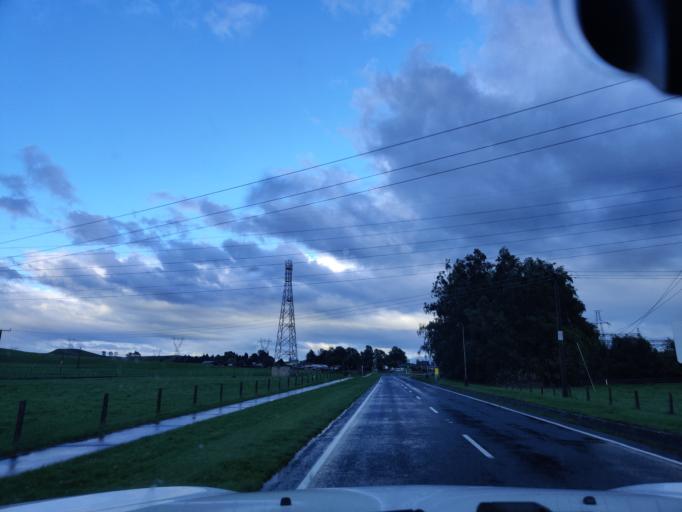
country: NZ
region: Waikato
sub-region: South Waikato District
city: Tokoroa
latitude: -38.4206
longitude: 175.8025
